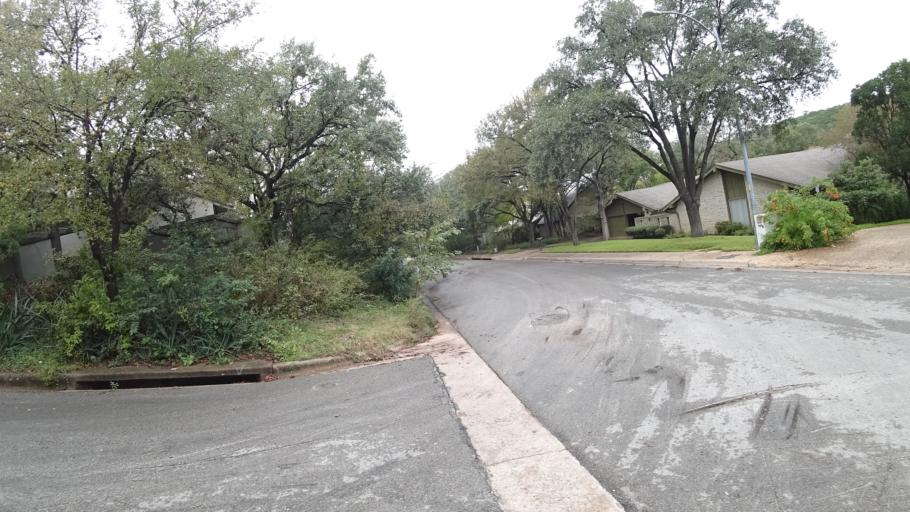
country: US
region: Texas
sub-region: Travis County
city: Rollingwood
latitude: 30.2611
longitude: -97.7824
